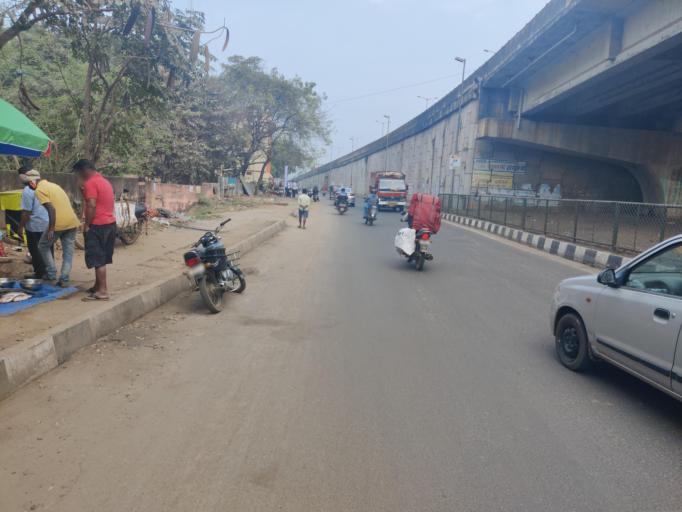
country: IN
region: Odisha
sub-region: Cuttack
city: Cuttack
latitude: 20.3636
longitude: 85.8909
